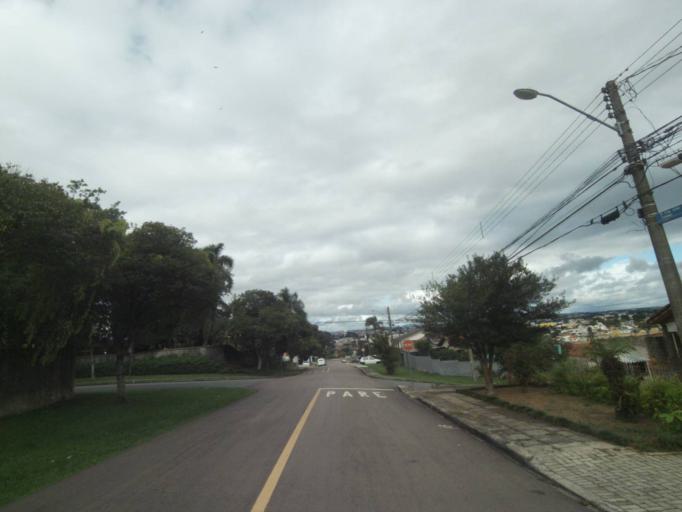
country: BR
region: Parana
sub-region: Curitiba
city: Curitiba
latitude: -25.4755
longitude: -49.2706
